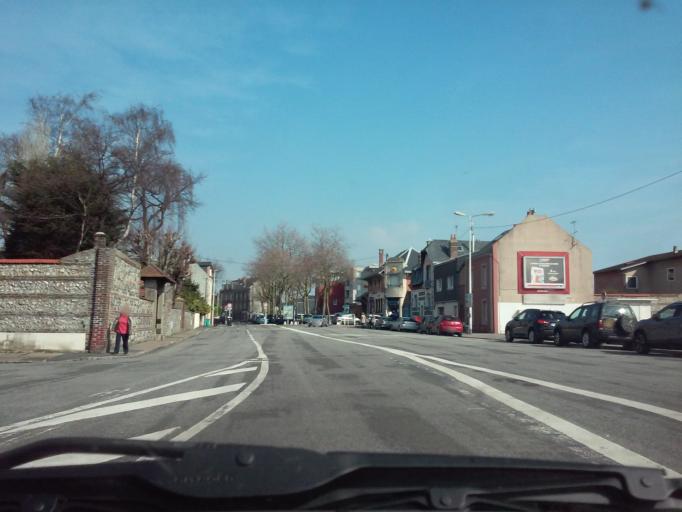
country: FR
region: Haute-Normandie
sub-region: Departement de la Seine-Maritime
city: Le Havre
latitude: 49.5056
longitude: 0.1024
